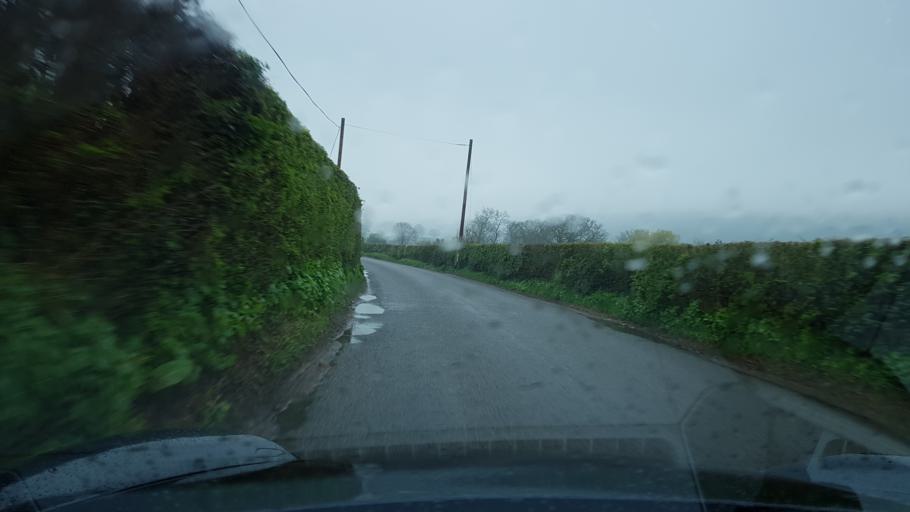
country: GB
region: England
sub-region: Gloucestershire
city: Mitcheldean
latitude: 51.8829
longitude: -2.4844
